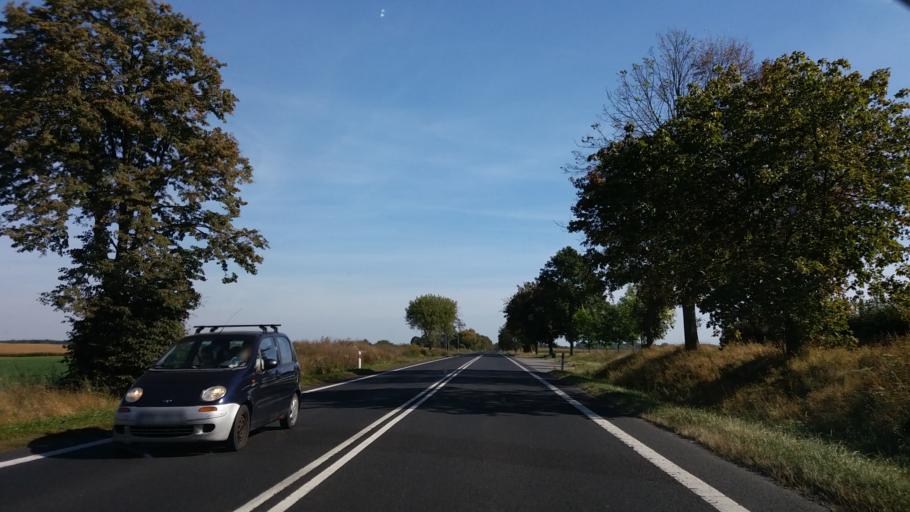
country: PL
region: Greater Poland Voivodeship
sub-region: Powiat miedzychodzki
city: Kwilcz
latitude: 52.5640
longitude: 16.0329
